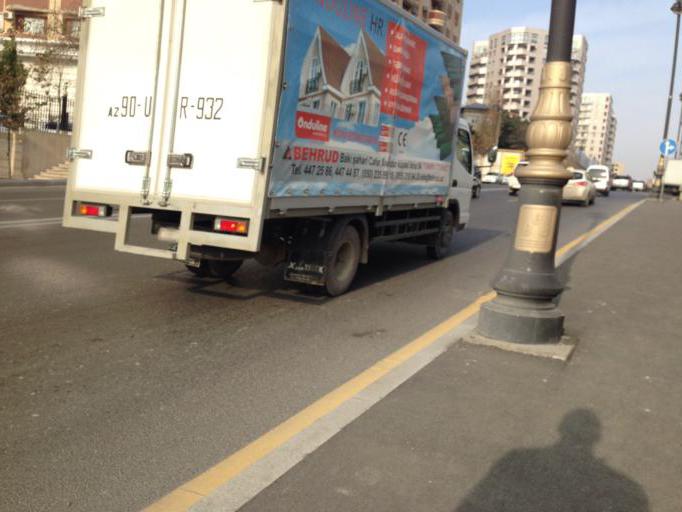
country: AZ
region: Baki
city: Baku
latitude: 40.3968
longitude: 49.8599
